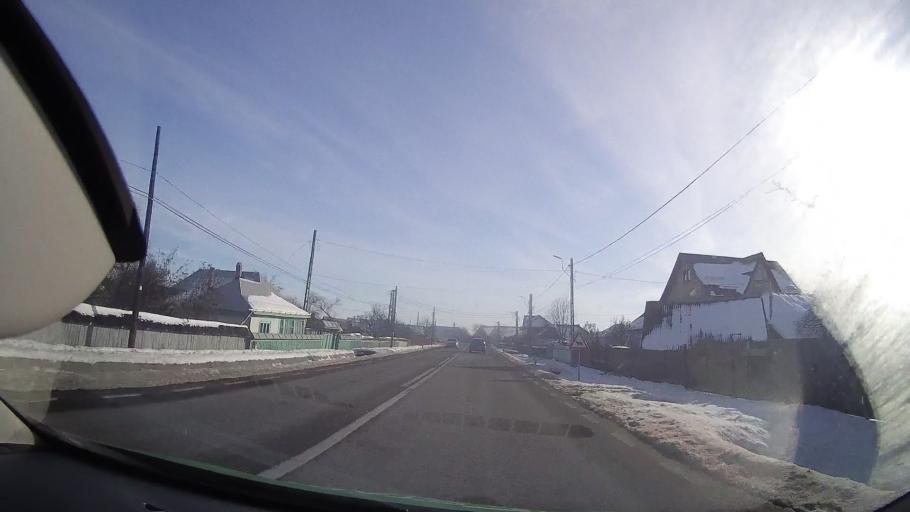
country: RO
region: Neamt
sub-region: Comuna Cracaoani
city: Cracaoani
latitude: 47.0904
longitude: 26.3237
